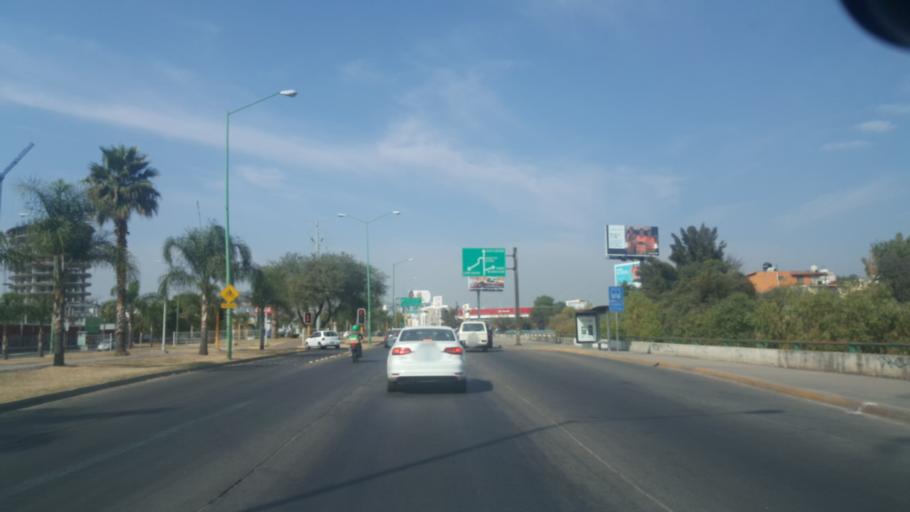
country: MX
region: Guanajuato
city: Leon
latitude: 21.1545
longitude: -101.6827
